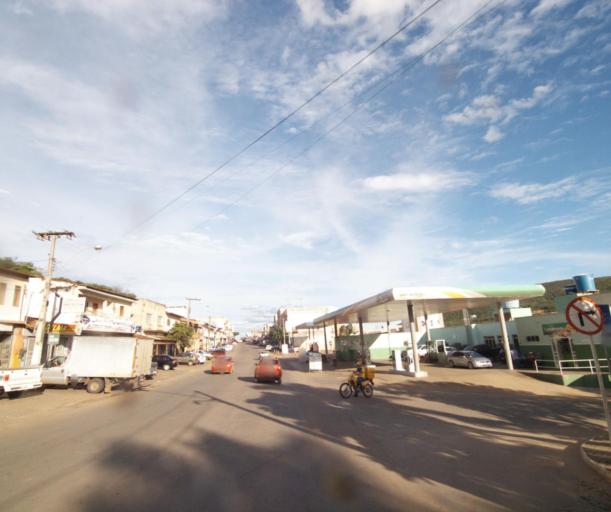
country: BR
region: Bahia
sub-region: Caetite
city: Caetite
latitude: -14.0653
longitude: -42.4845
